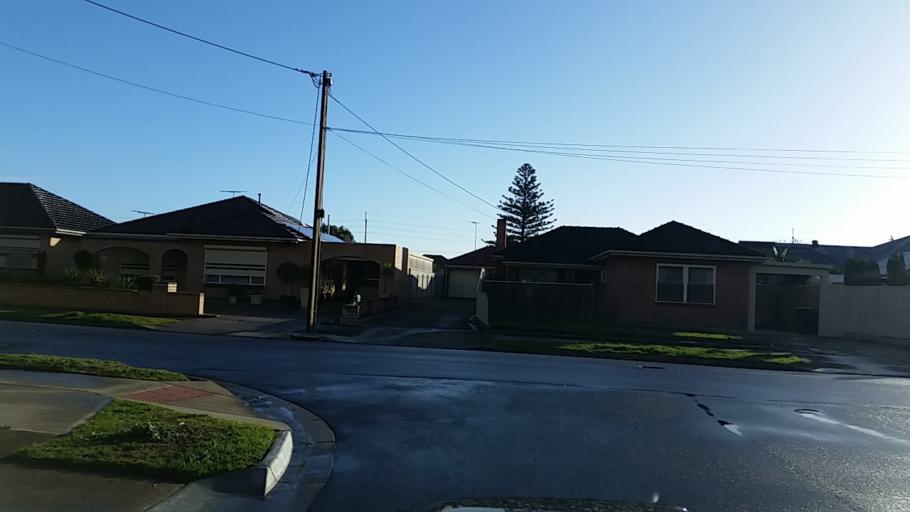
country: AU
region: South Australia
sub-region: Charles Sturt
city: Findon
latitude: -34.8996
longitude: 138.5347
